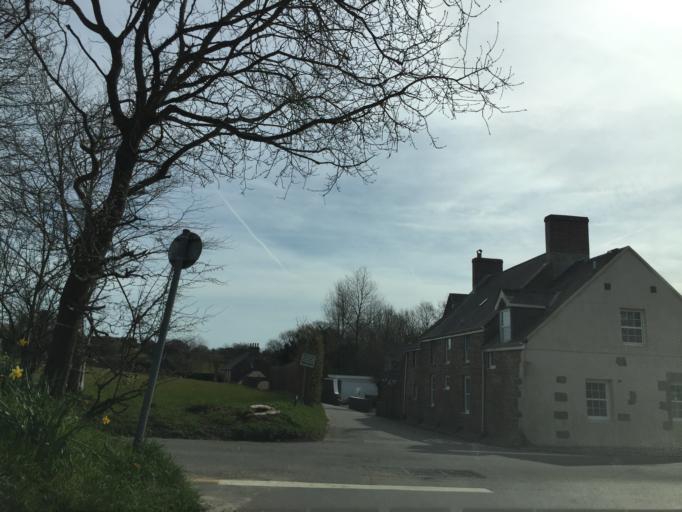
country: JE
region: St Helier
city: Saint Helier
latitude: 49.2279
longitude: -2.1234
